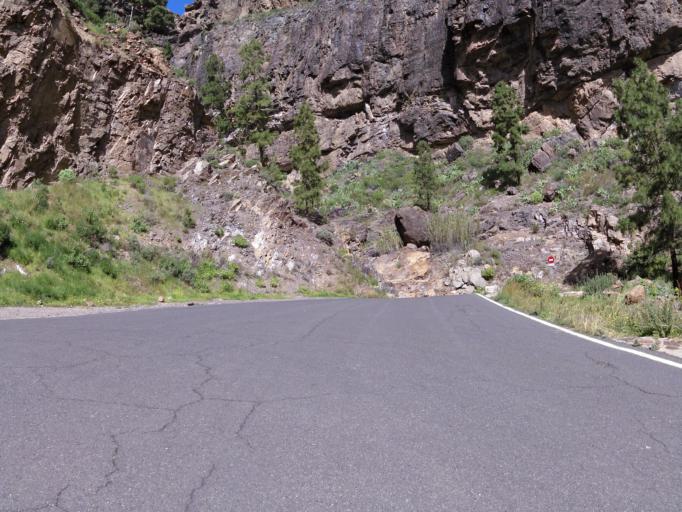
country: ES
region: Canary Islands
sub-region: Provincia de Las Palmas
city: Mogan
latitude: 27.9157
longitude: -15.6690
